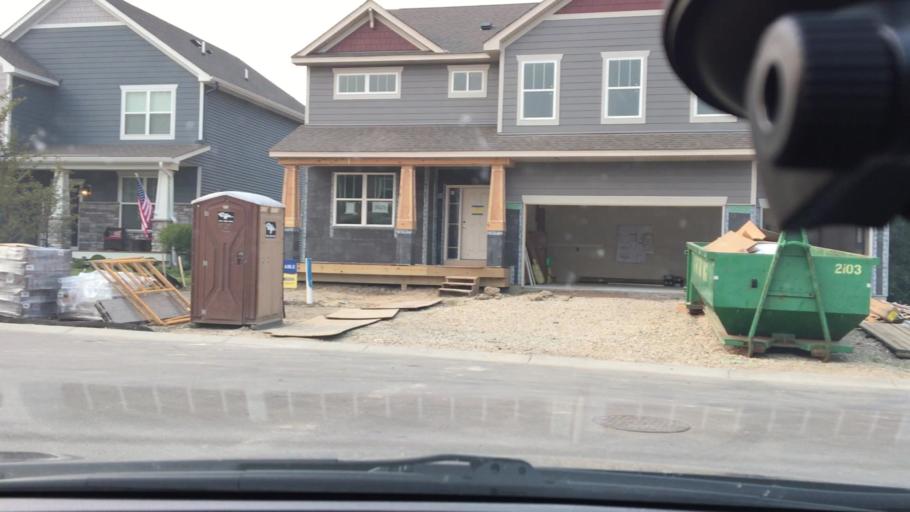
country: US
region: Minnesota
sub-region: Wright County
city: Saint Michael
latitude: 45.2054
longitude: -93.6810
